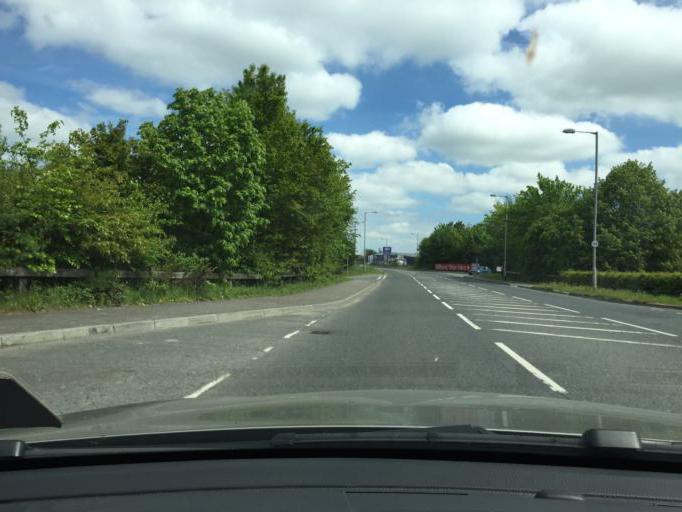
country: GB
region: Northern Ireland
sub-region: Armagh District
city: Portadown
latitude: 54.4485
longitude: -6.4227
